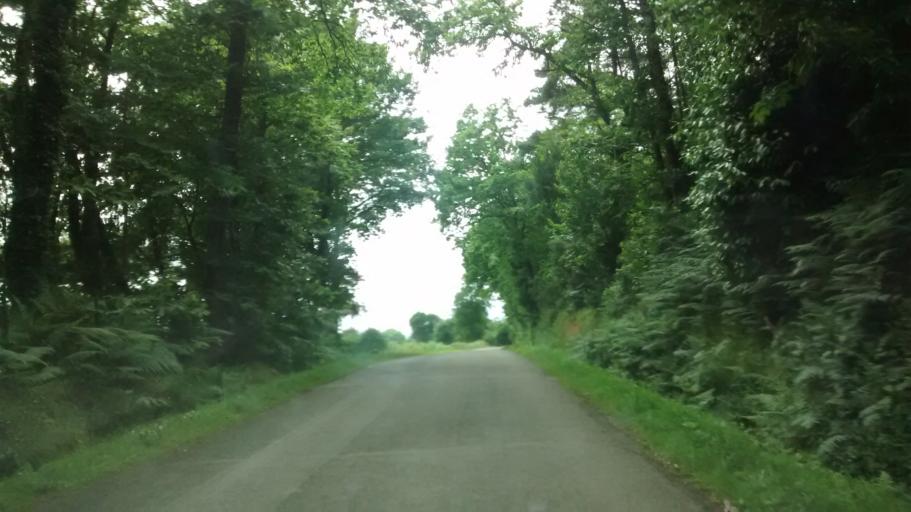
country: FR
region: Brittany
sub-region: Departement du Morbihan
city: Ruffiac
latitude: 47.8432
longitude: -2.2111
